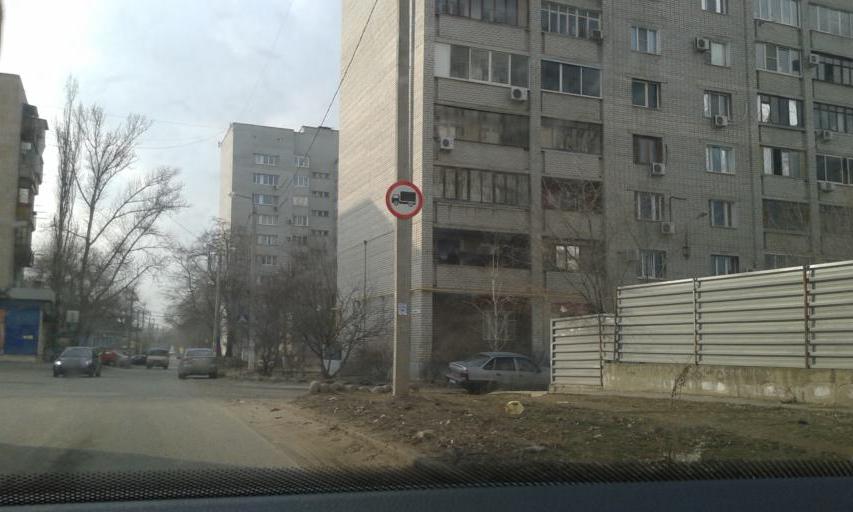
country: RU
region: Volgograd
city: Volgograd
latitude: 48.6552
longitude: 44.4313
